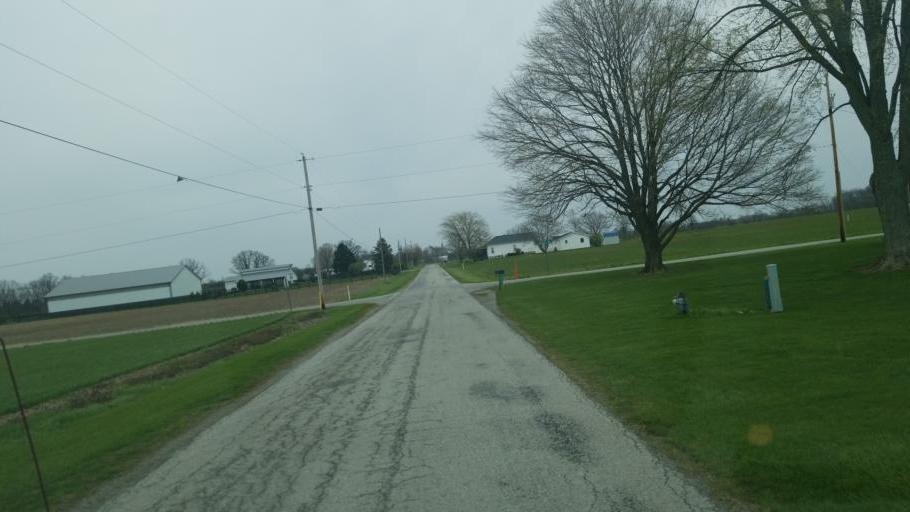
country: US
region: Ohio
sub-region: Wyandot County
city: Carey
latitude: 40.9748
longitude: -83.5045
